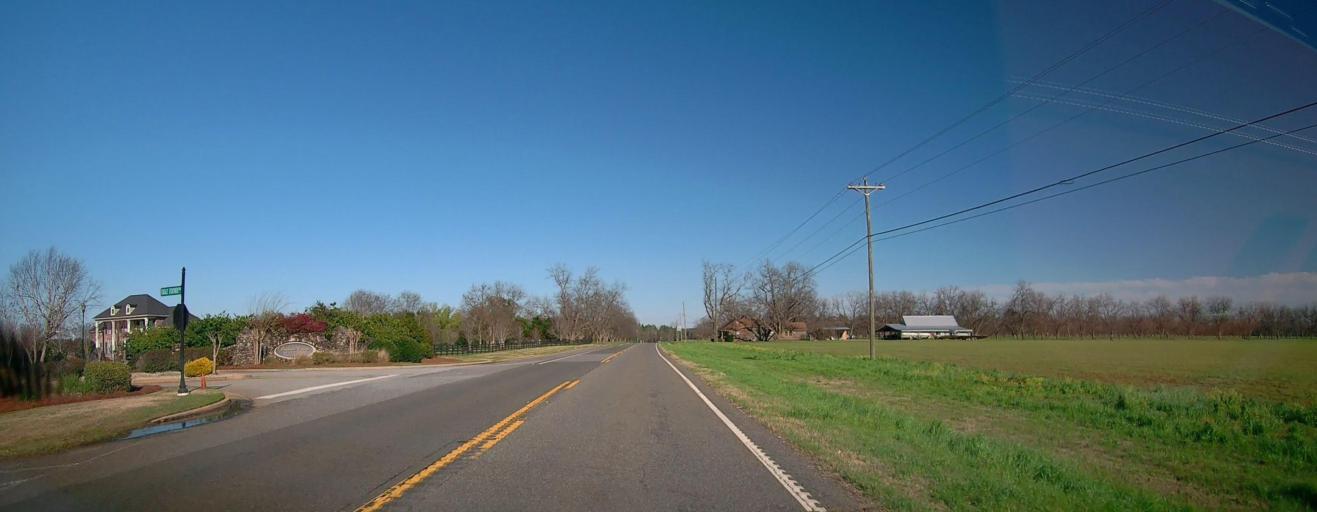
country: US
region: Georgia
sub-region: Houston County
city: Perry
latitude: 32.4409
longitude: -83.8061
